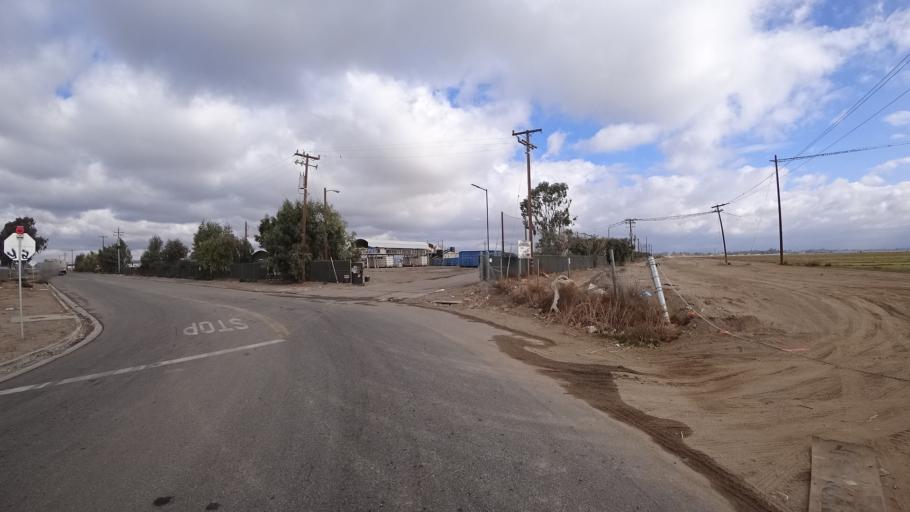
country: US
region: California
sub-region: Kern County
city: Greenfield
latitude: 35.3251
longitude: -118.9678
